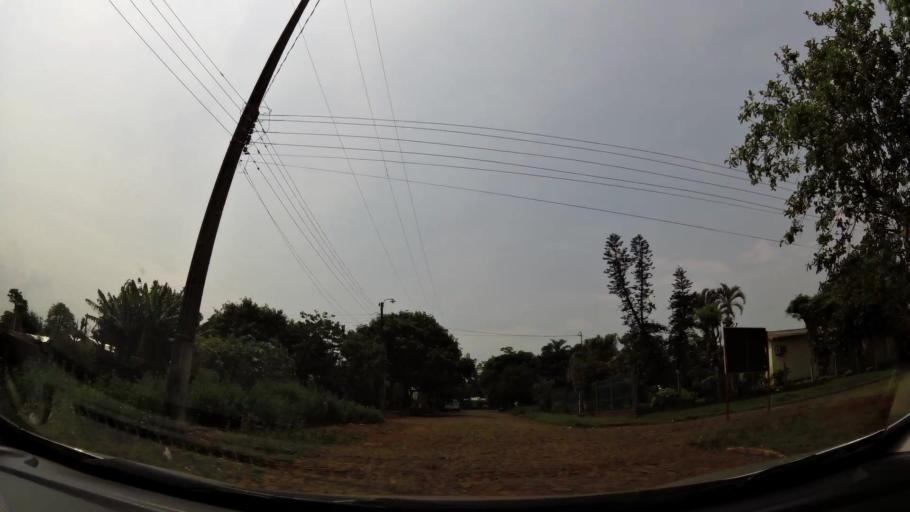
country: PY
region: Alto Parana
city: Presidente Franco
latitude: -25.5681
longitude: -54.6171
